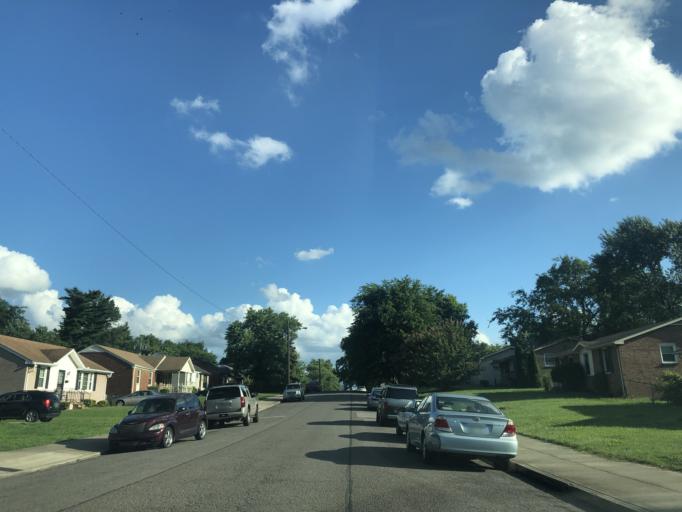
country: US
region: Tennessee
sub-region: Davidson County
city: Nashville
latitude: 36.1862
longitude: -86.7722
